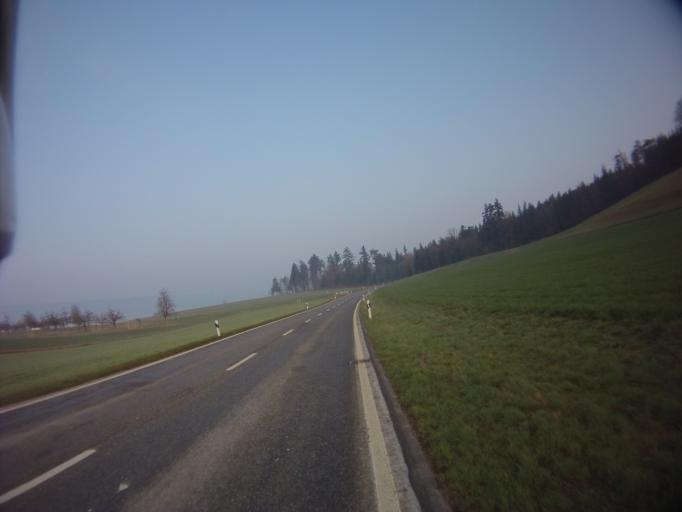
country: CH
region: Zurich
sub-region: Bezirk Affoltern
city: Obfelden
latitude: 47.2413
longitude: 8.4274
